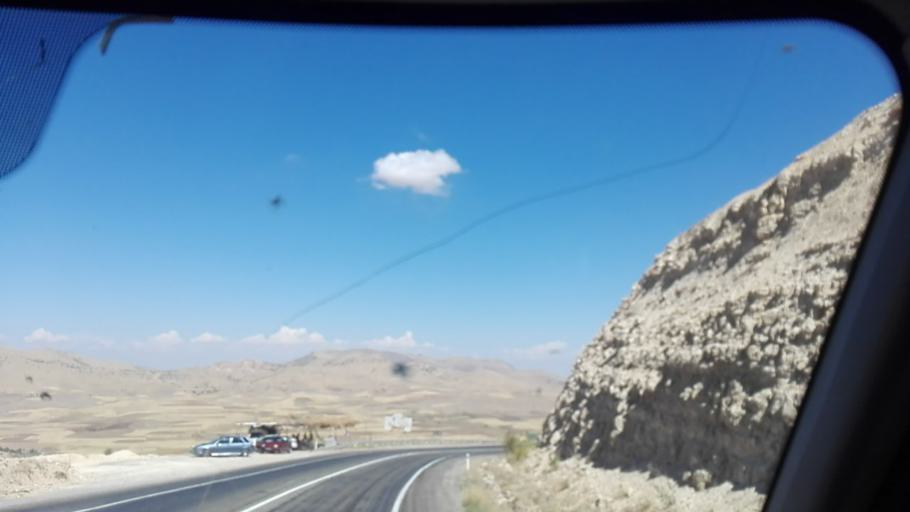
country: TR
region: Batman
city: Gerdzhyush
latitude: 37.5607
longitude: 41.3607
